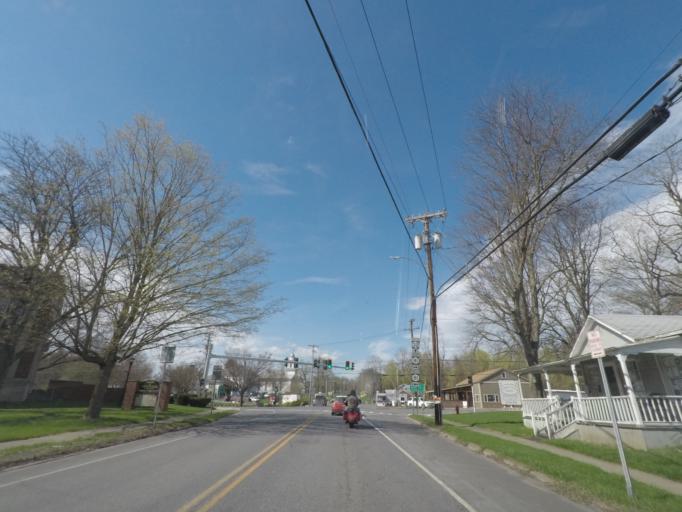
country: US
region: New York
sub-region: Greene County
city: Cairo
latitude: 42.4149
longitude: -74.0220
